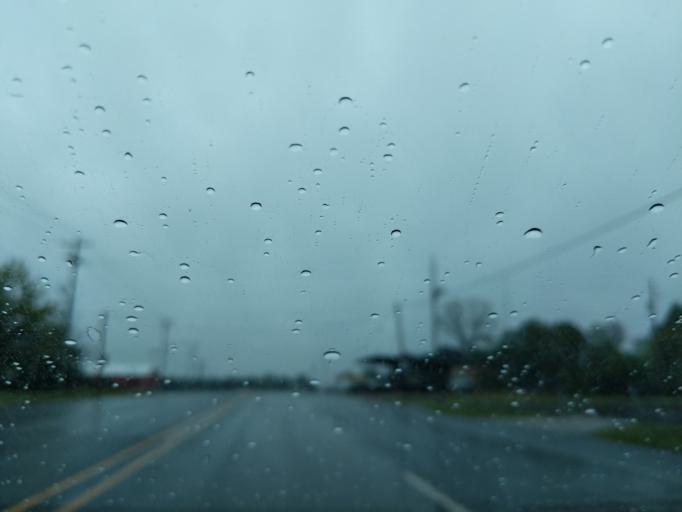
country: US
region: Texas
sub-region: Panola County
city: Carthage
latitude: 32.1576
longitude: -94.3284
